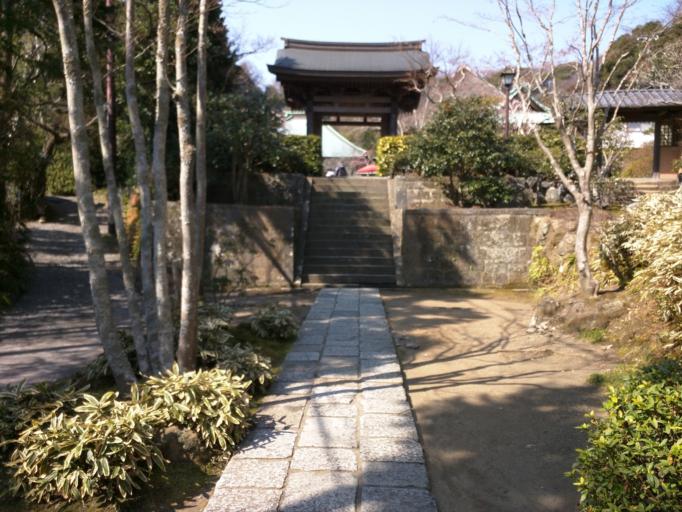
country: JP
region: Kanagawa
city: Kamakura
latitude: 35.3286
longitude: 139.5458
